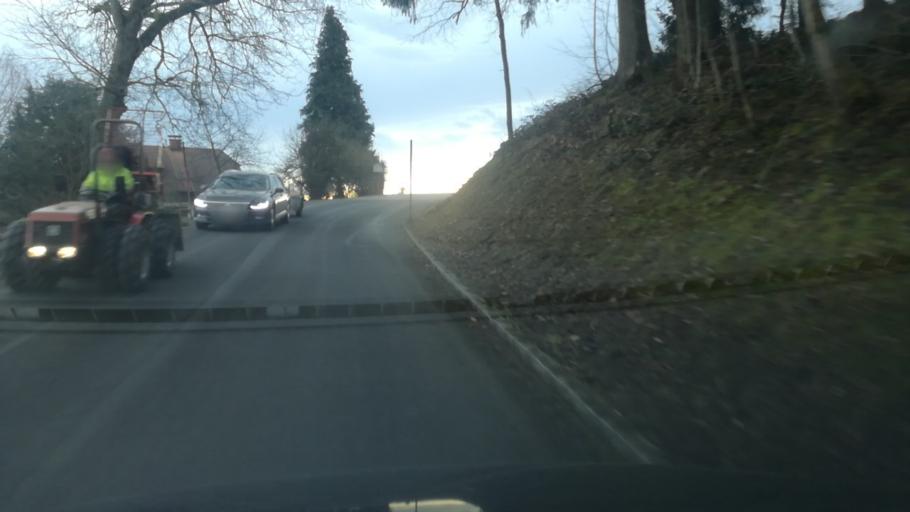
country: AT
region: Upper Austria
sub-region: Politischer Bezirk Vocklabruck
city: Neukirchen an der Vockla
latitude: 48.0487
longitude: 13.5387
